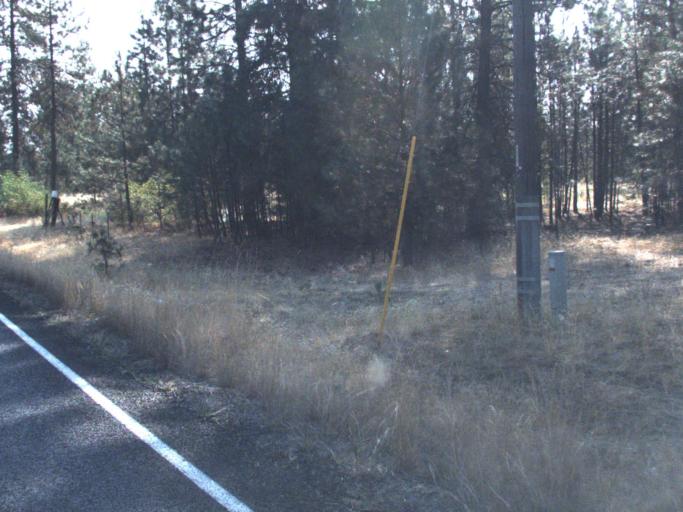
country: US
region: Washington
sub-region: Spokane County
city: Fairchild Air Force Base
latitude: 47.8392
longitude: -117.7778
